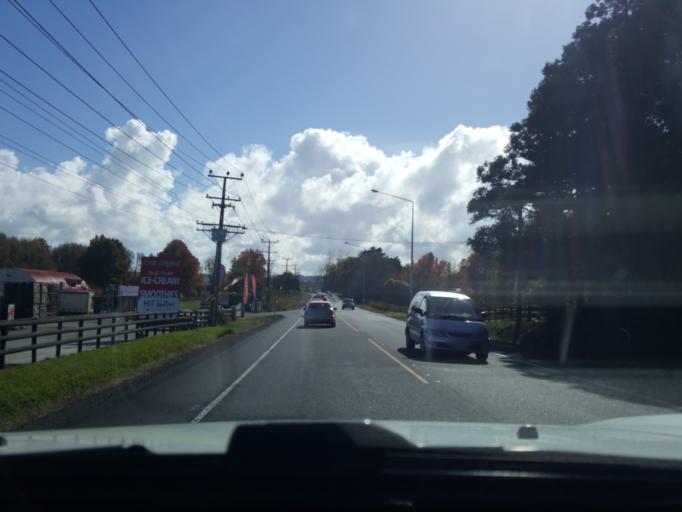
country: NZ
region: Auckland
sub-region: Auckland
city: Muriwai Beach
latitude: -36.7840
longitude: 174.5714
